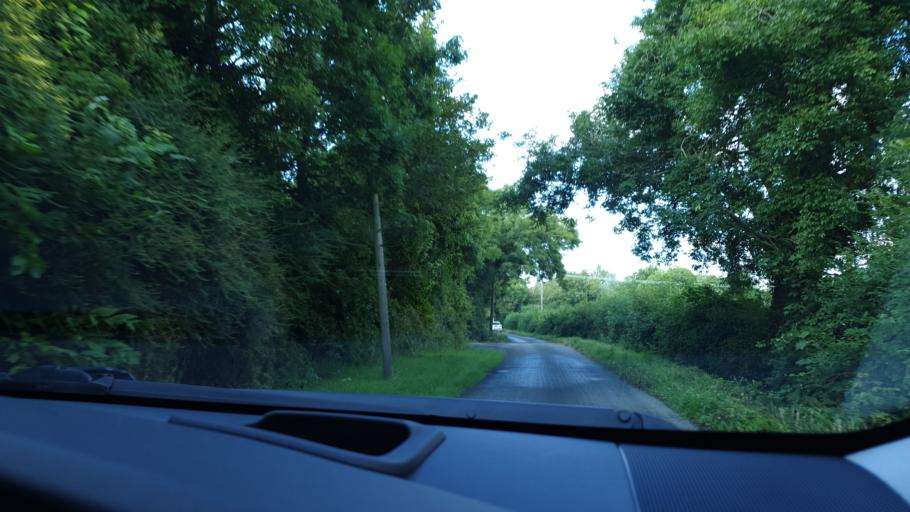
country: IE
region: Leinster
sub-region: An Mhi
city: Ashbourne
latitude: 53.4943
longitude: -6.4044
